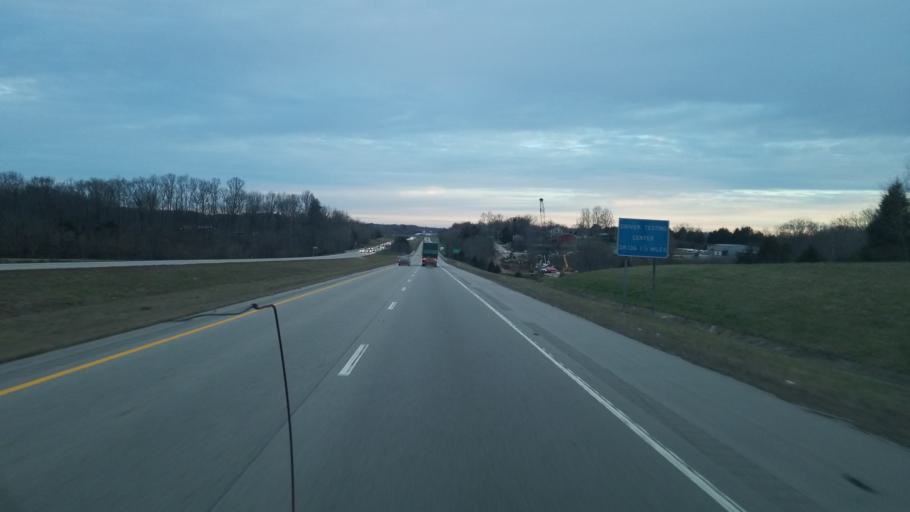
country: US
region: Tennessee
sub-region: Putnam County
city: Cookeville
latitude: 36.0788
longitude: -85.5066
